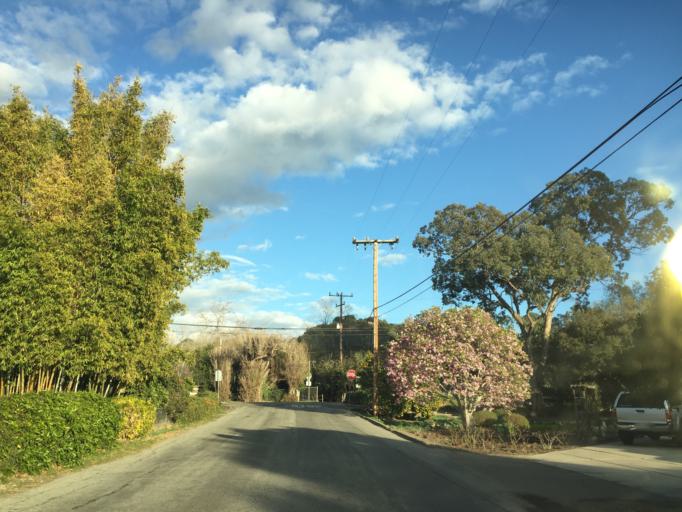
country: US
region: California
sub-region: Santa Barbara County
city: Goleta
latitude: 34.4364
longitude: -119.7718
